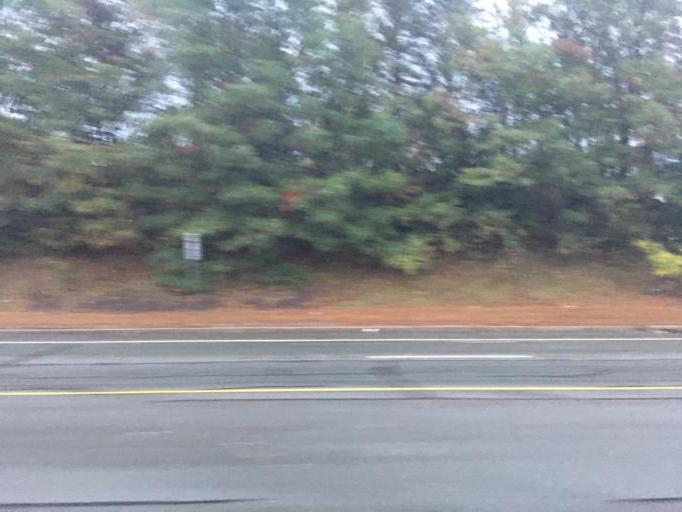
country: US
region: Rhode Island
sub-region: Kent County
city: West Warwick
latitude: 41.6906
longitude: -71.5003
